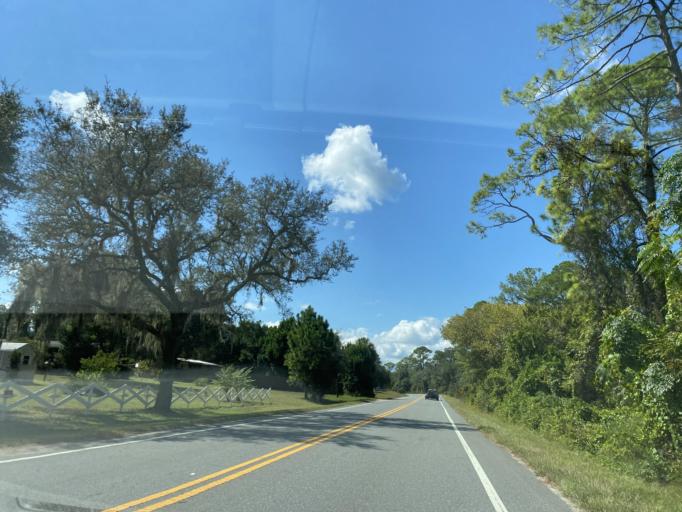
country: US
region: Florida
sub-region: Lake County
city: Lake Mack-Forest Hills
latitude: 29.0175
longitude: -81.4829
